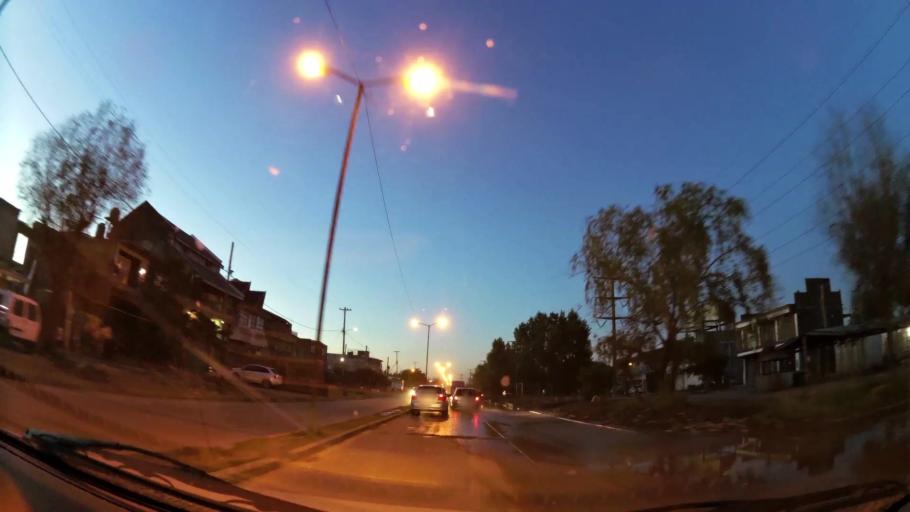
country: AR
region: Buenos Aires
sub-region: Partido de Almirante Brown
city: Adrogue
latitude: -34.7726
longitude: -58.3236
